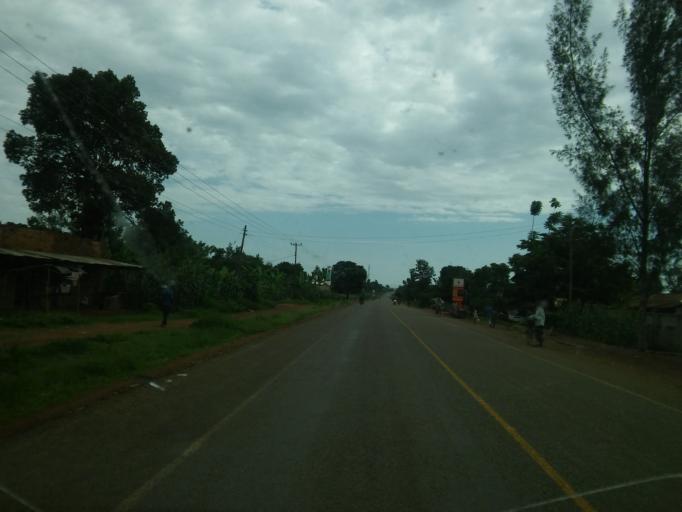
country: UG
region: Eastern Region
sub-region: Mbale District
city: Mbale
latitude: 1.1318
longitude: 34.1666
